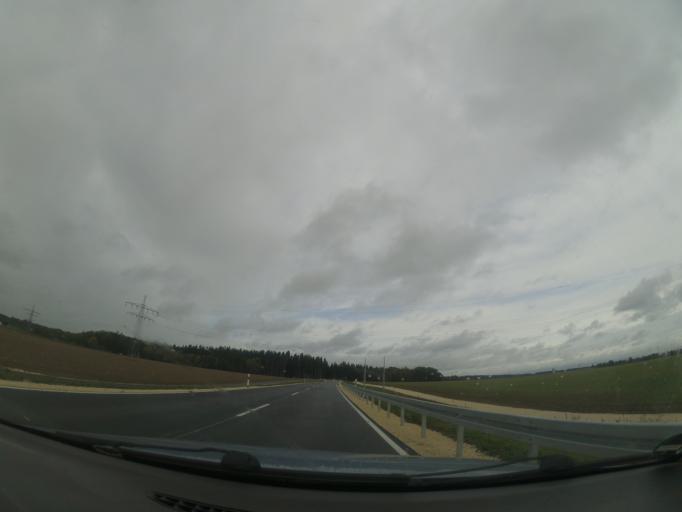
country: DE
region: Baden-Wuerttemberg
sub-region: Tuebingen Region
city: Beimerstetten
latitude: 48.4720
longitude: 9.9677
